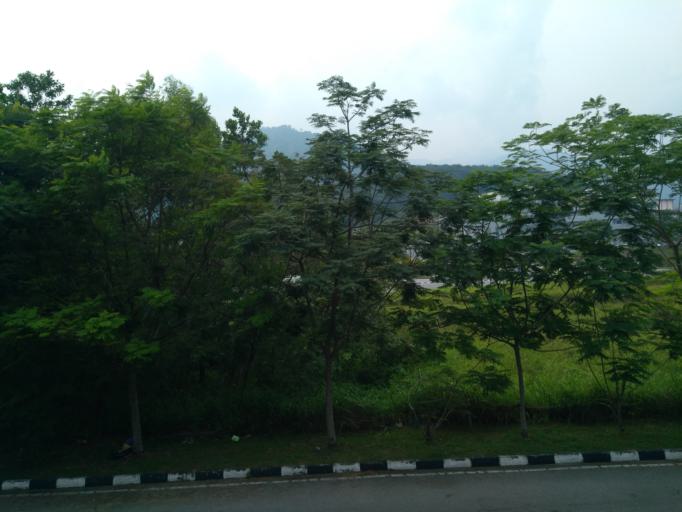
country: MY
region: Perak
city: Ipoh
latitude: 4.6701
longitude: 101.0728
